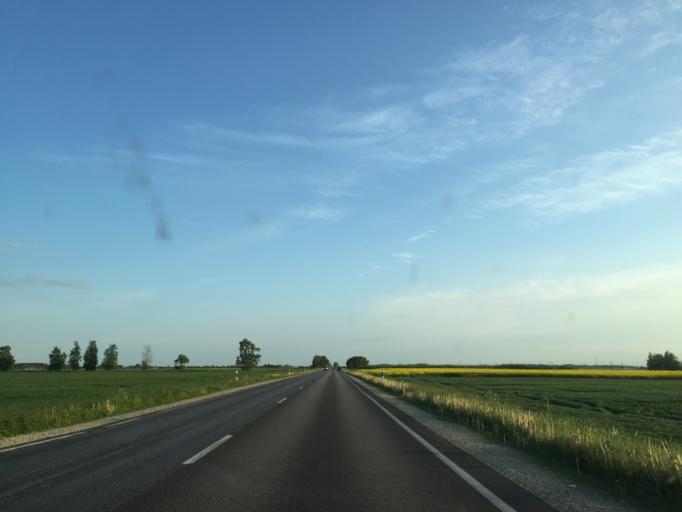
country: LT
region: Siauliu apskritis
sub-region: Joniskis
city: Joniskis
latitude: 56.0926
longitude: 23.4719
